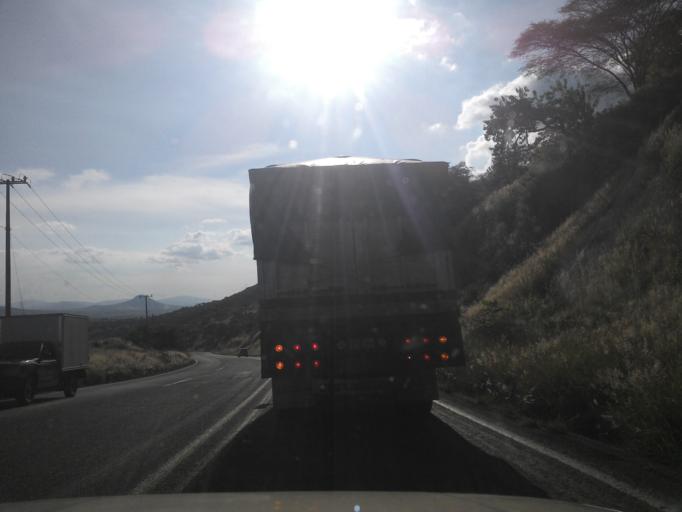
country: MX
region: Jalisco
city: Atotonilco el Alto
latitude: 20.5545
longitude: -102.5166
